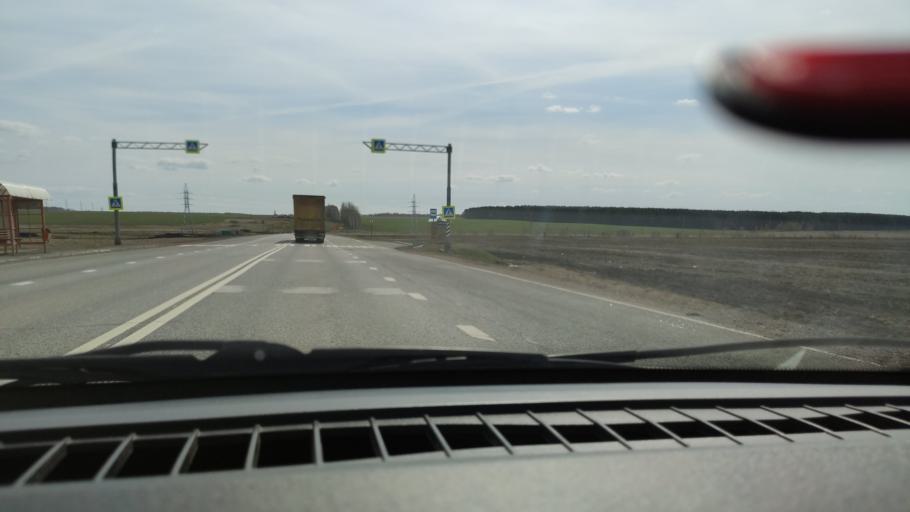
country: RU
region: Bashkortostan
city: Dyurtyuli
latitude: 55.2952
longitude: 55.0195
